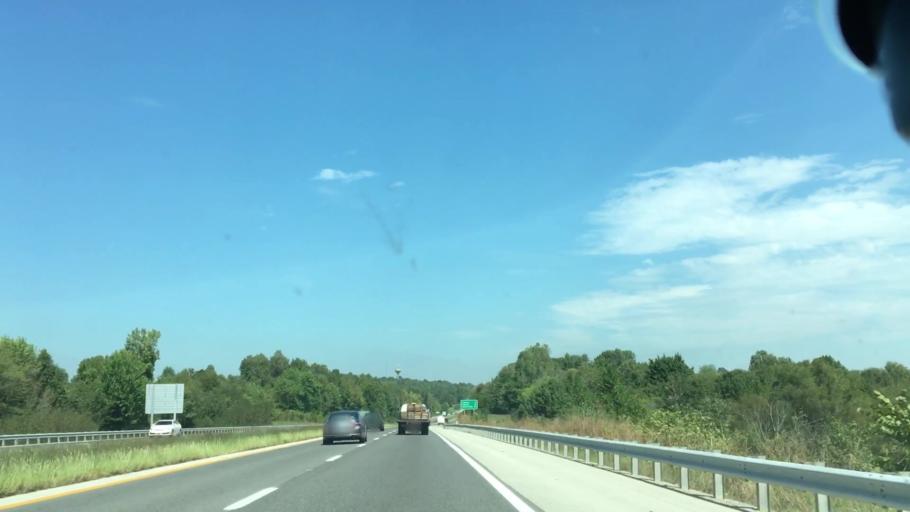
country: US
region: Kentucky
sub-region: Hopkins County
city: Madisonville
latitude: 37.3698
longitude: -87.4885
